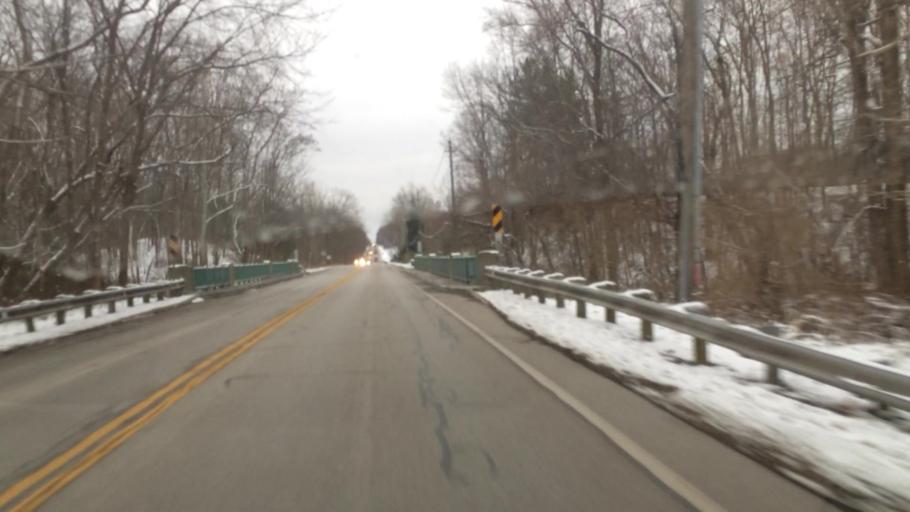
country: US
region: Ohio
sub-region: Cuyahoga County
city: Strongsville
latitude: 41.3098
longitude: -81.7854
